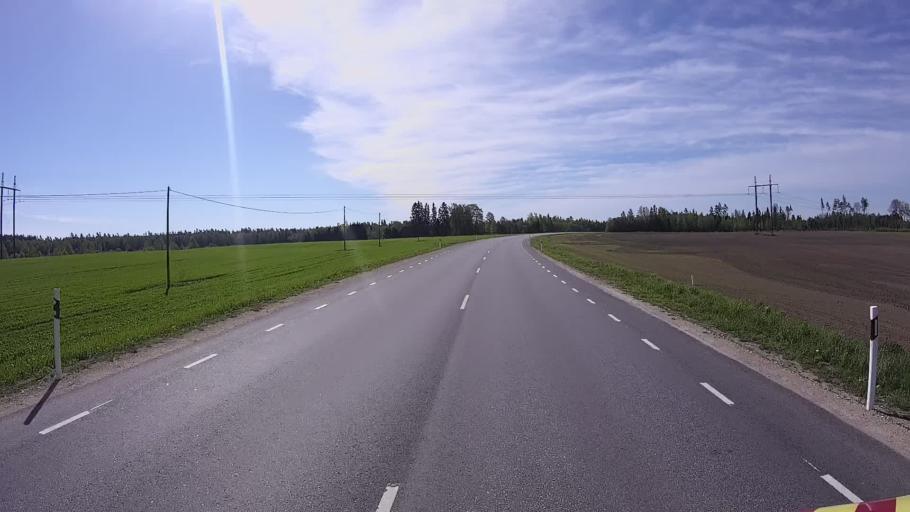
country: EE
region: Polvamaa
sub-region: Polva linn
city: Polva
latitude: 58.3103
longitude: 26.9959
